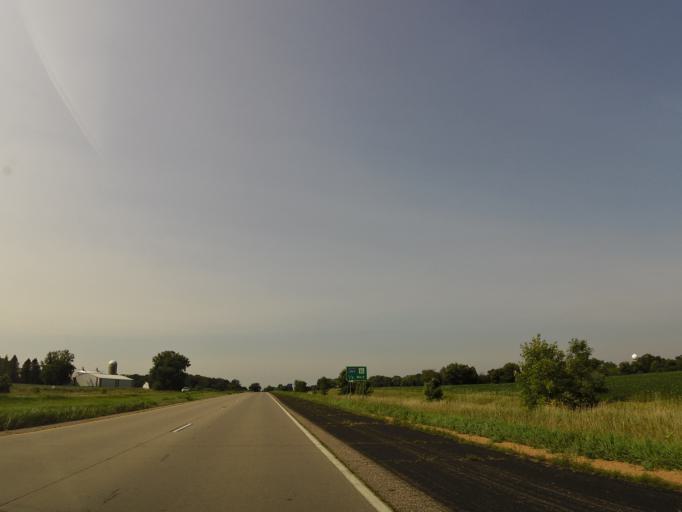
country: US
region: Minnesota
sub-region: Carver County
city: Cologne
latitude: 44.7695
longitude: -93.7701
